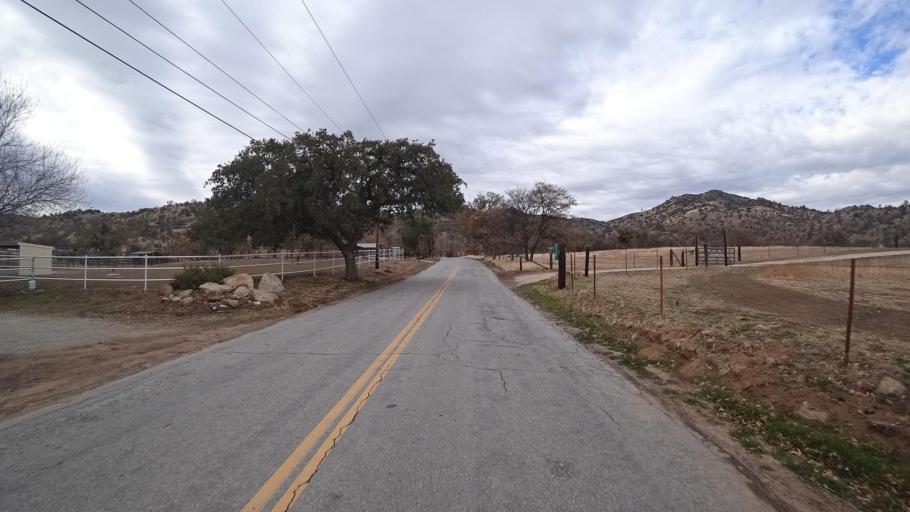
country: US
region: California
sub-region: Kern County
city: Golden Hills
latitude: 35.1264
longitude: -118.5102
